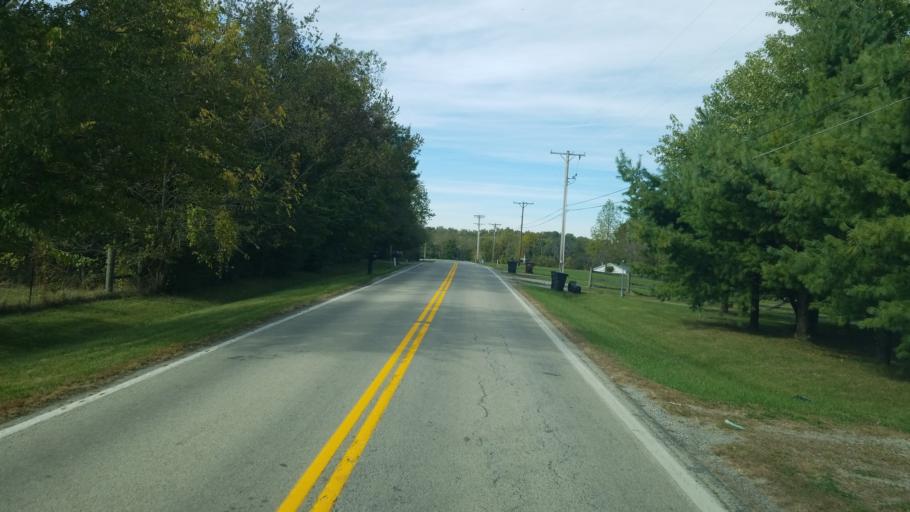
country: US
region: Ohio
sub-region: Highland County
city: Leesburg
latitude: 39.3381
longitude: -83.5941
